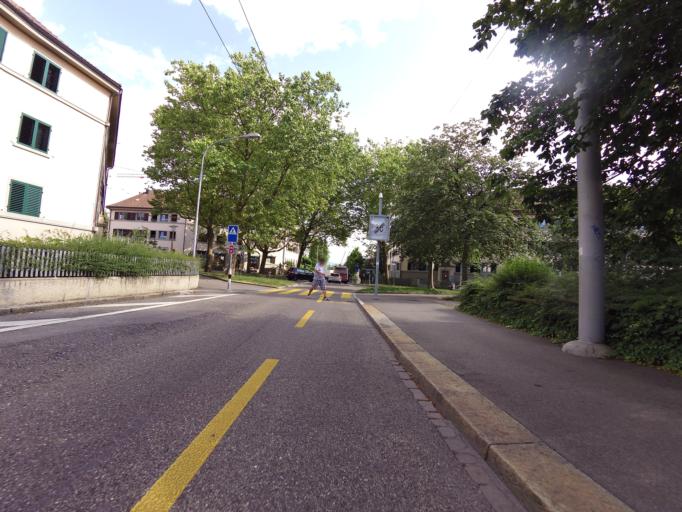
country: CH
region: Zurich
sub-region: Bezirk Zuerich
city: Zuerich (Kreis 5) / Gewerbeschule
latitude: 47.3889
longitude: 8.5339
